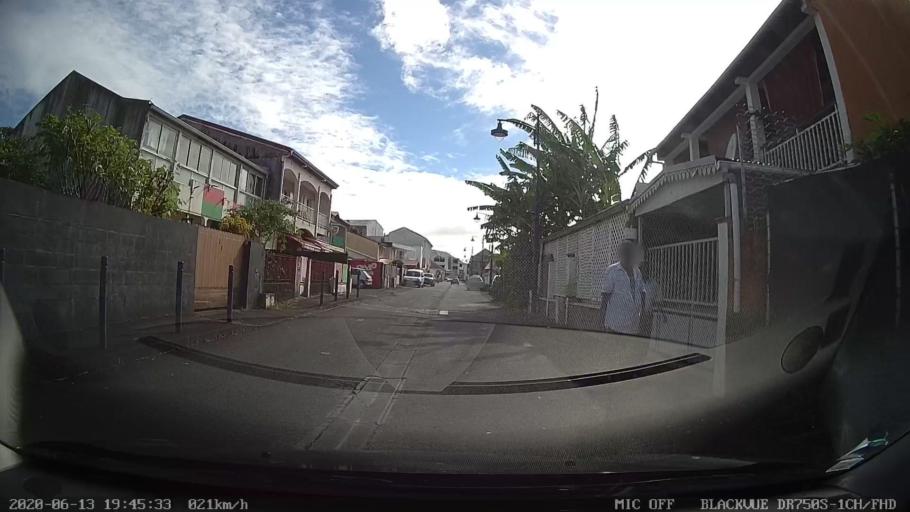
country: RE
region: Reunion
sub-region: Reunion
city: Bras-Panon
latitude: -20.9969
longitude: 55.6771
